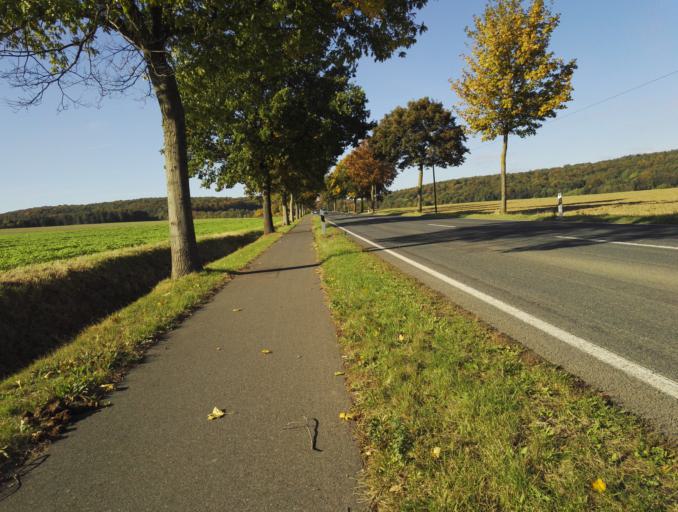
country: DE
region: Lower Saxony
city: Holle
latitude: 52.1155
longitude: 10.1031
